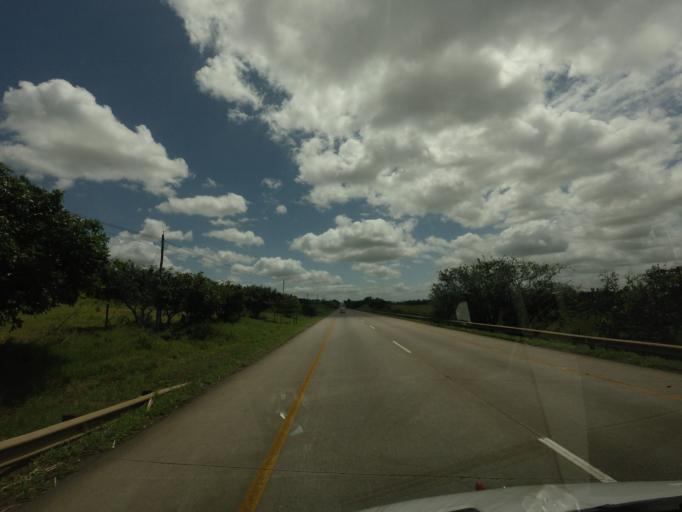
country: ZA
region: KwaZulu-Natal
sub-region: uMkhanyakude District Municipality
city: Mtubatuba
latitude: -28.4859
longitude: 32.1421
